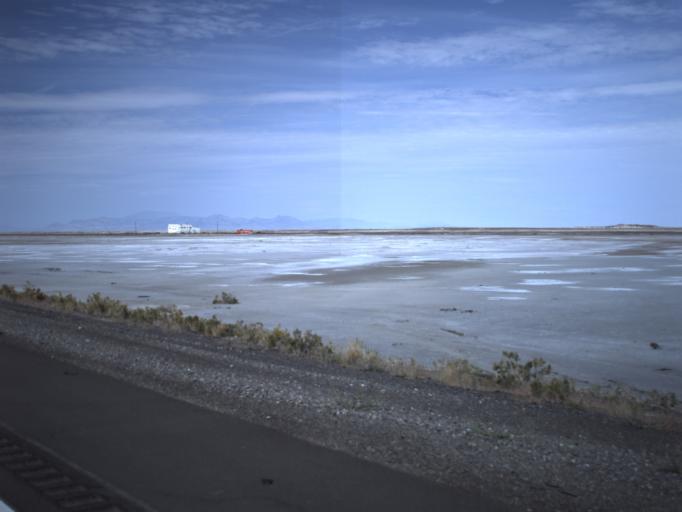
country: US
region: Utah
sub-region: Tooele County
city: Wendover
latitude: 40.7277
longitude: -113.2853
